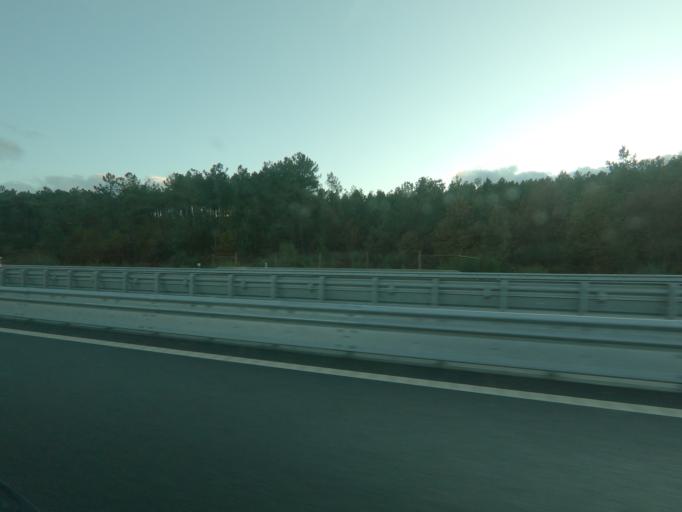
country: PT
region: Vila Real
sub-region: Santa Marta de Penaguiao
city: Santa Marta de Penaguiao
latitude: 41.2766
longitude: -7.8210
